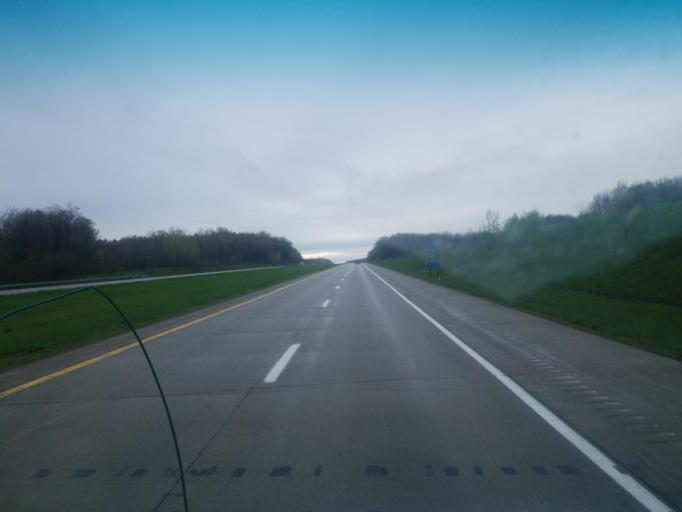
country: US
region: Pennsylvania
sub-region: Erie County
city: North East
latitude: 42.1480
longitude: -79.8489
